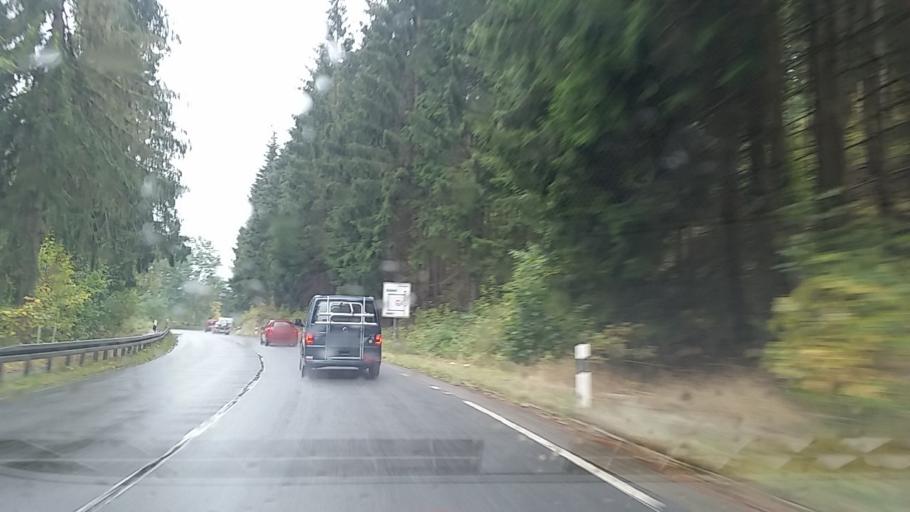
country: DE
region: Lower Saxony
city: Schulenberg im Oberharz
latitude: 51.8464
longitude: 10.4516
